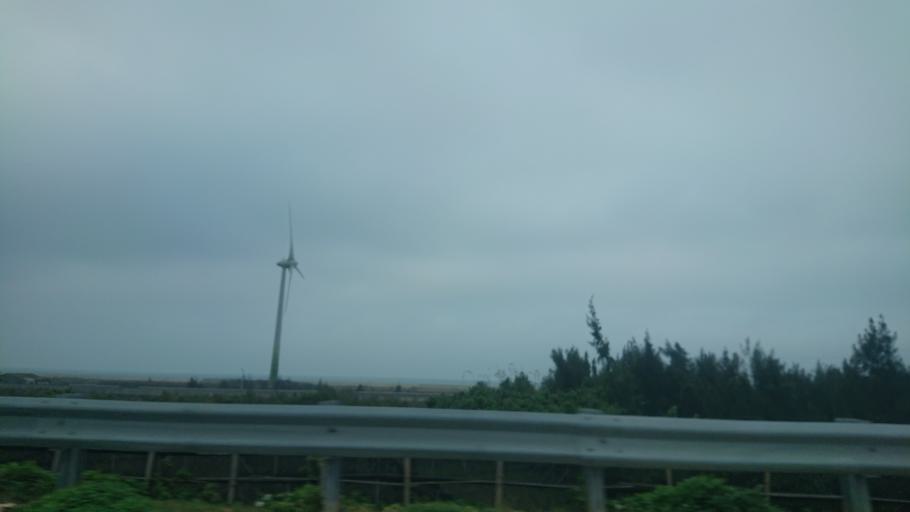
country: TW
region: Taiwan
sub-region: Miaoli
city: Miaoli
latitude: 24.5122
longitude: 120.6845
